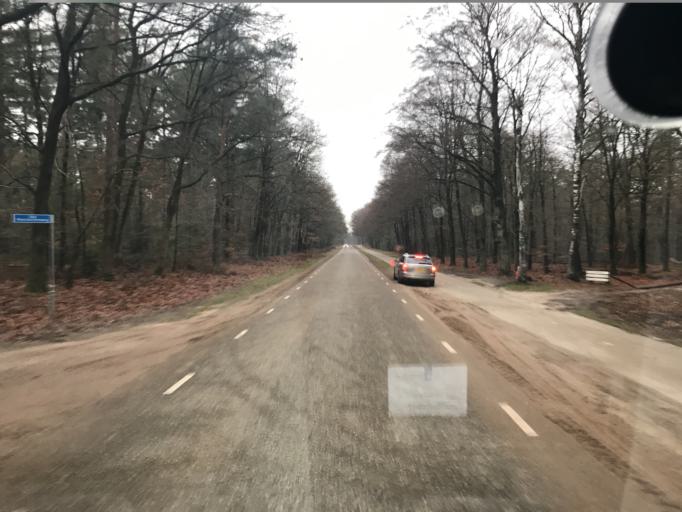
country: NL
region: Gelderland
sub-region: Gemeente Apeldoorn
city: Beekbergen
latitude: 52.1859
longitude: 5.9055
